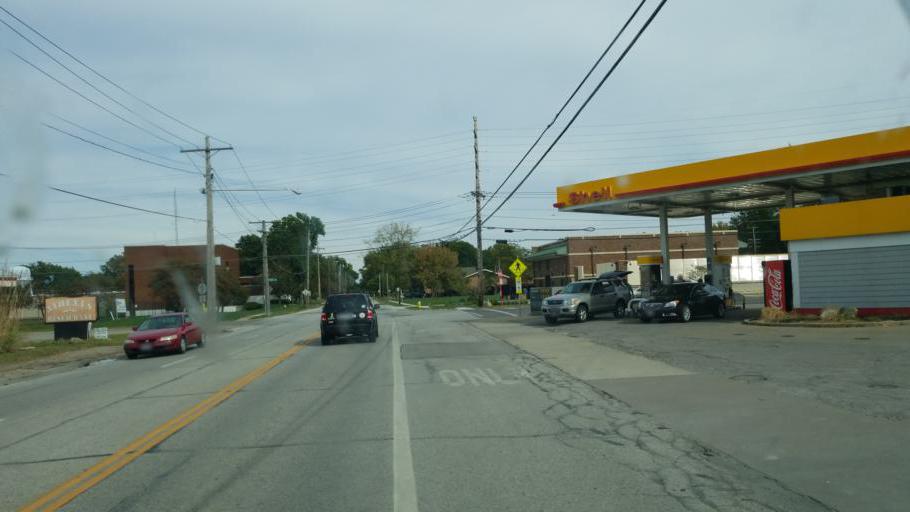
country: US
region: Ohio
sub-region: Lorain County
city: Avon Lake
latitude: 41.5050
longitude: -82.0474
